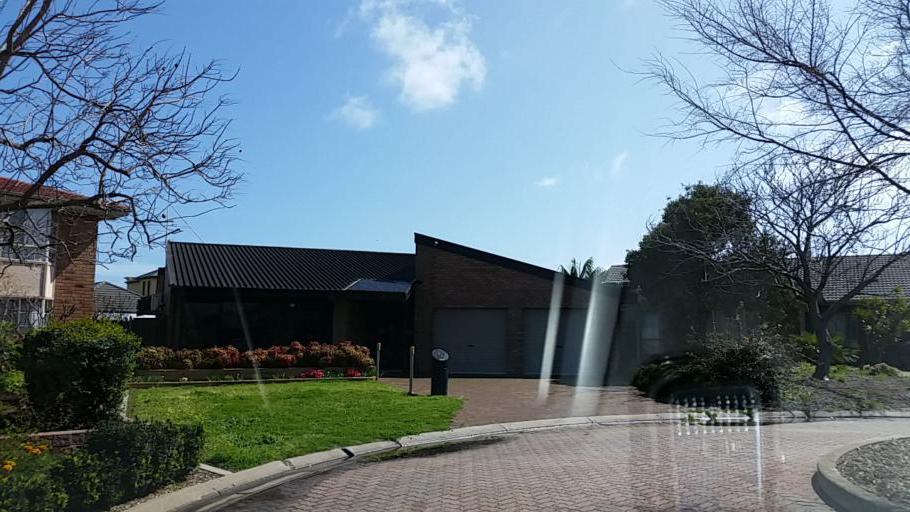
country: AU
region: South Australia
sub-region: Charles Sturt
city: Grange
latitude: -34.8982
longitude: 138.5043
